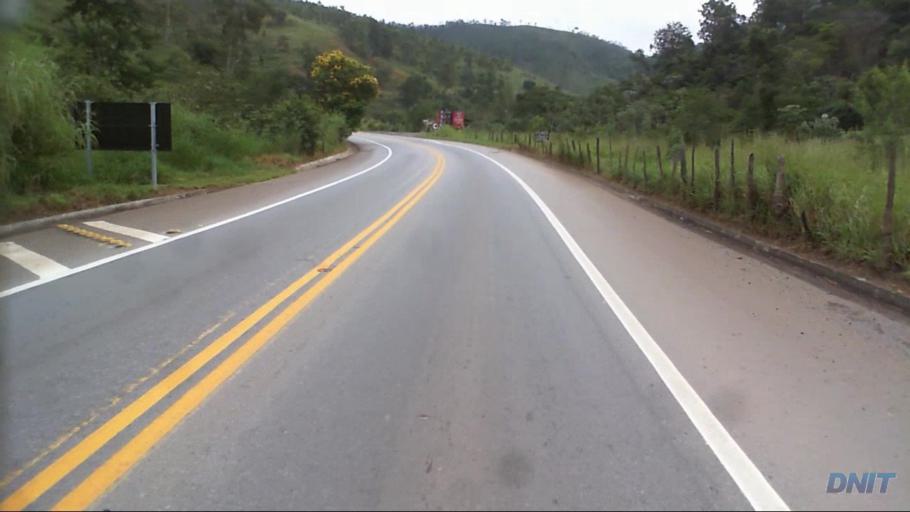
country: BR
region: Minas Gerais
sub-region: Timoteo
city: Timoteo
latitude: -19.6367
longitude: -42.8267
